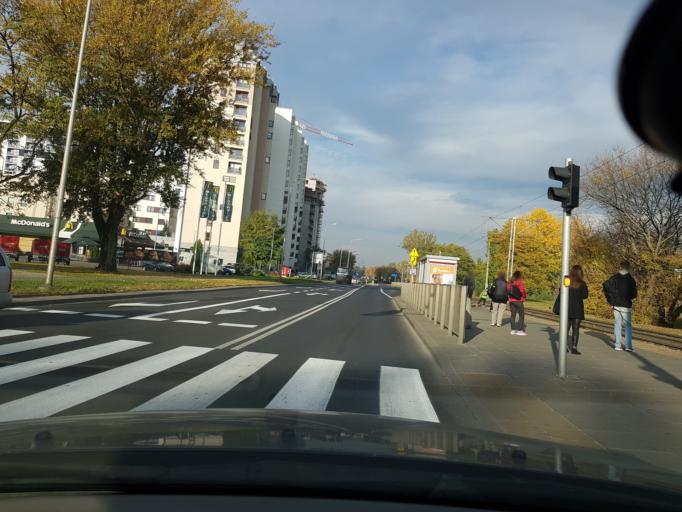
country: PL
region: Masovian Voivodeship
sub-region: Warszawa
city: Bielany
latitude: 52.2812
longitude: 20.9242
